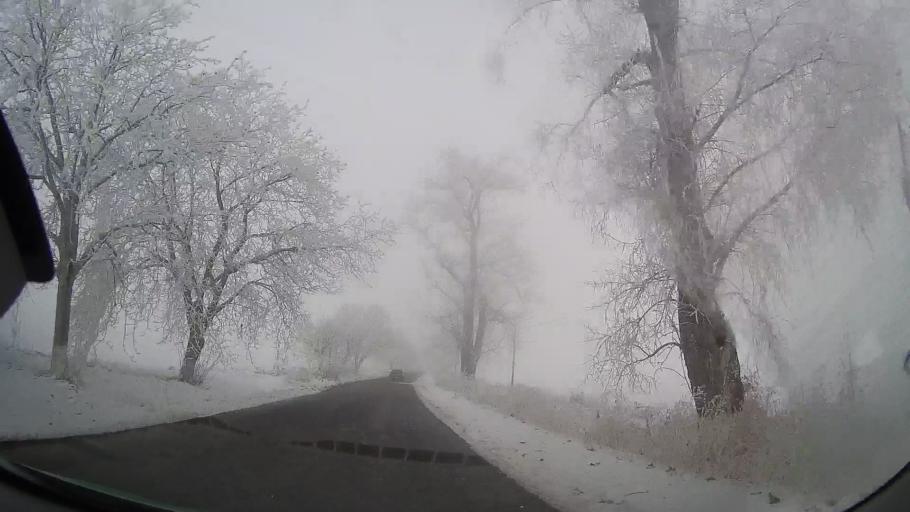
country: RO
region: Neamt
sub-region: Comuna Sabaoani
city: Sabaoani
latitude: 46.9878
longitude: 26.8632
